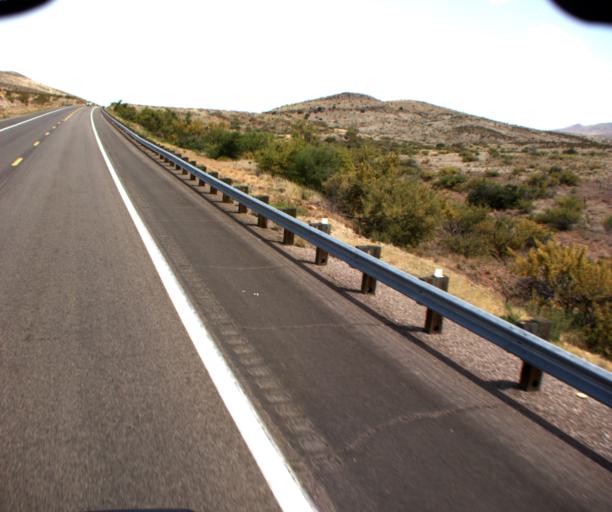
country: US
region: Arizona
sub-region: Greenlee County
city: Clifton
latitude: 32.7408
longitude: -109.2060
